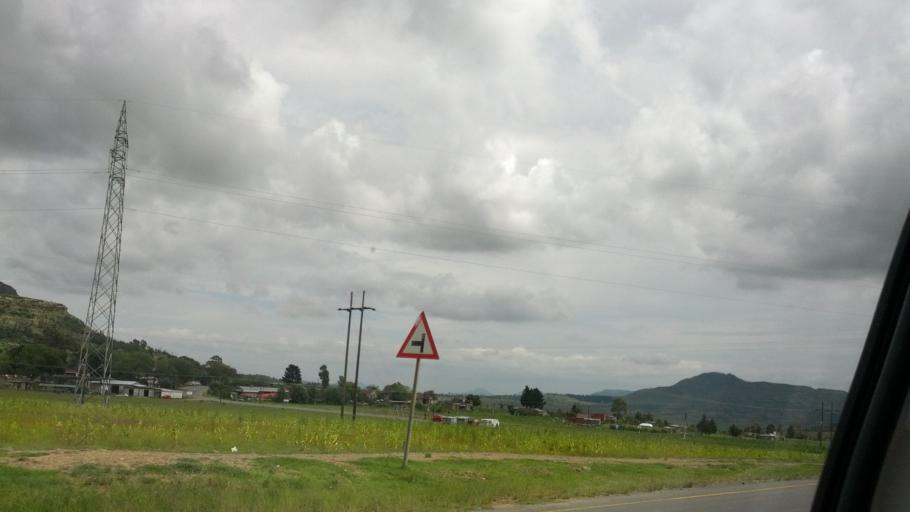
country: LS
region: Maseru
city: Nako
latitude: -29.5930
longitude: 27.4961
